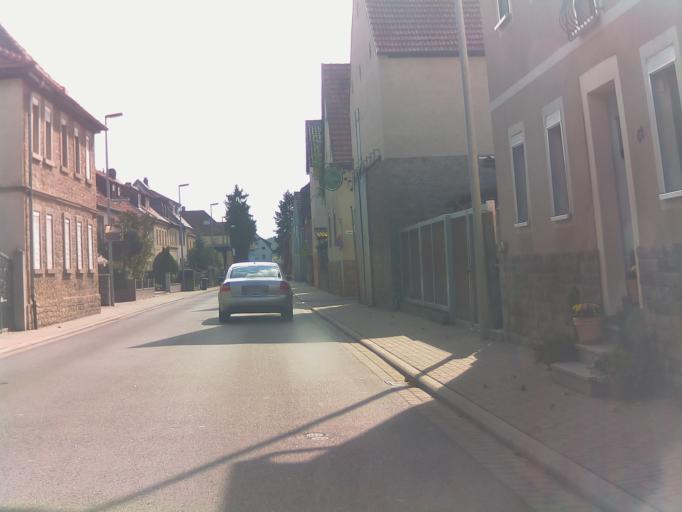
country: DE
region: Bavaria
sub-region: Regierungsbezirk Unterfranken
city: Mainstockheim
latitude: 49.7720
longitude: 10.1521
